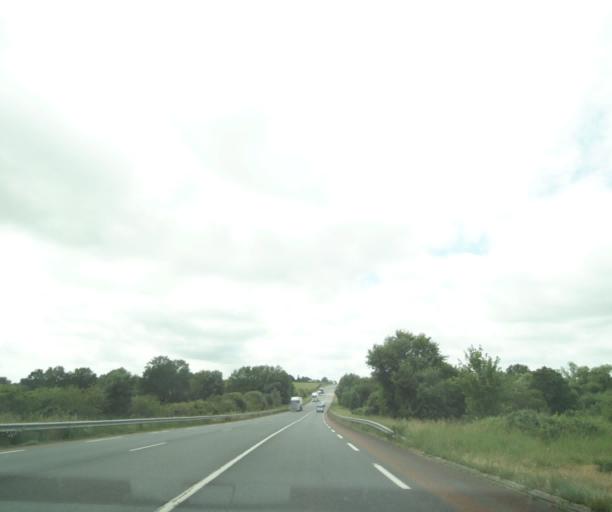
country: FR
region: Poitou-Charentes
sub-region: Departement des Deux-Sevres
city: Viennay
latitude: 46.7567
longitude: -0.2227
